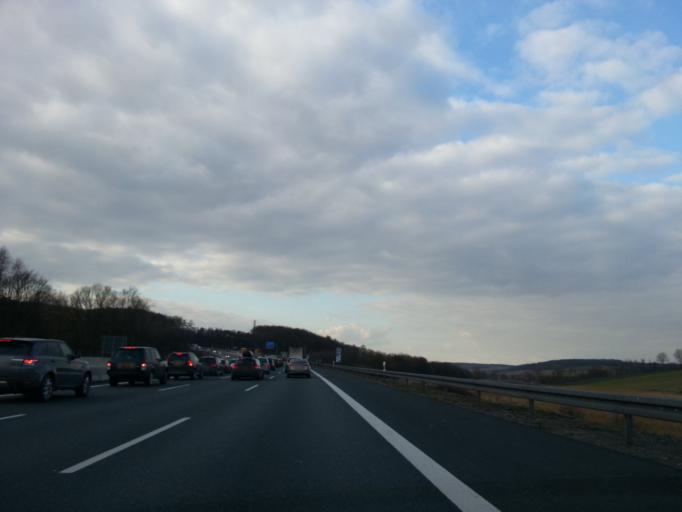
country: DE
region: Bavaria
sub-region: Regierungsbezirk Unterfranken
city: Waldbrunn
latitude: 49.7640
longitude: 9.7789
